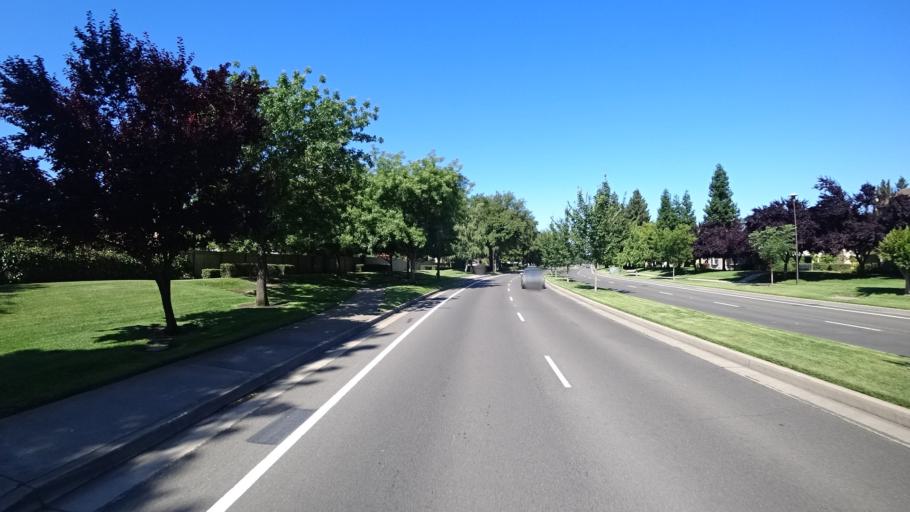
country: US
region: California
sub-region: Sacramento County
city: Parkway
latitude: 38.4764
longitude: -121.5247
